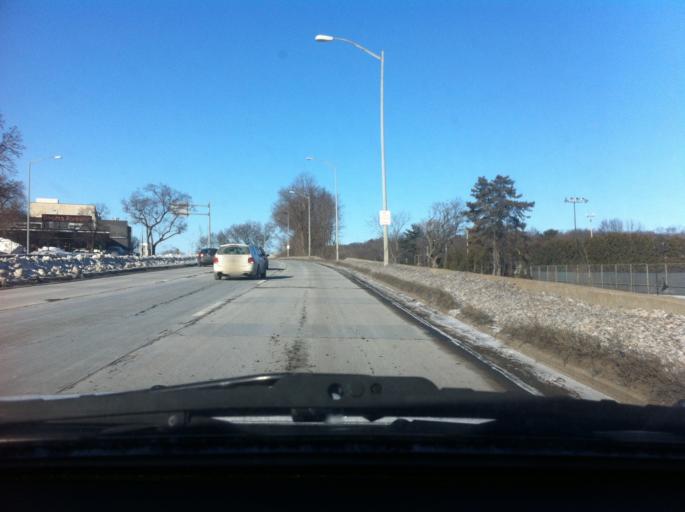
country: US
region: Wisconsin
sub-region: Dane County
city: Shorewood Hills
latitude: 43.0749
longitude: -89.4388
